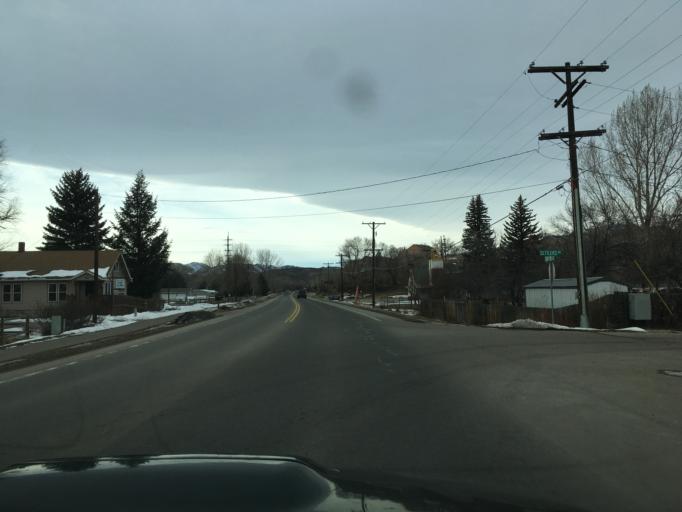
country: US
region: Colorado
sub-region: Larimer County
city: Laporte
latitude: 40.6300
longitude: -105.1467
